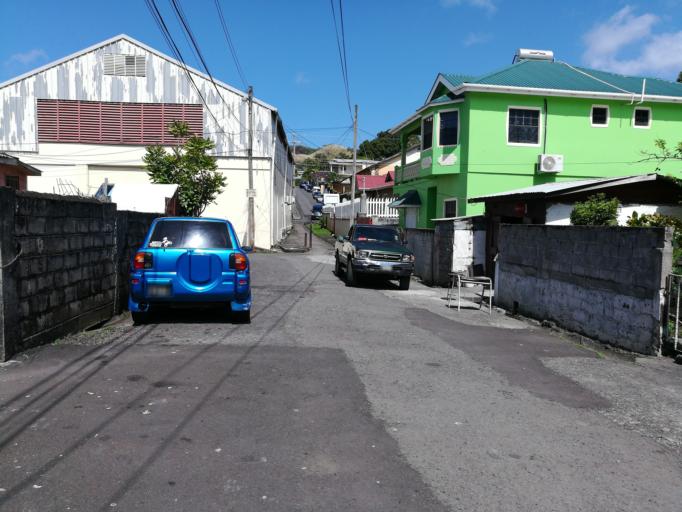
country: VC
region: Saint George
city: Kingstown
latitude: 13.1574
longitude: -61.2255
